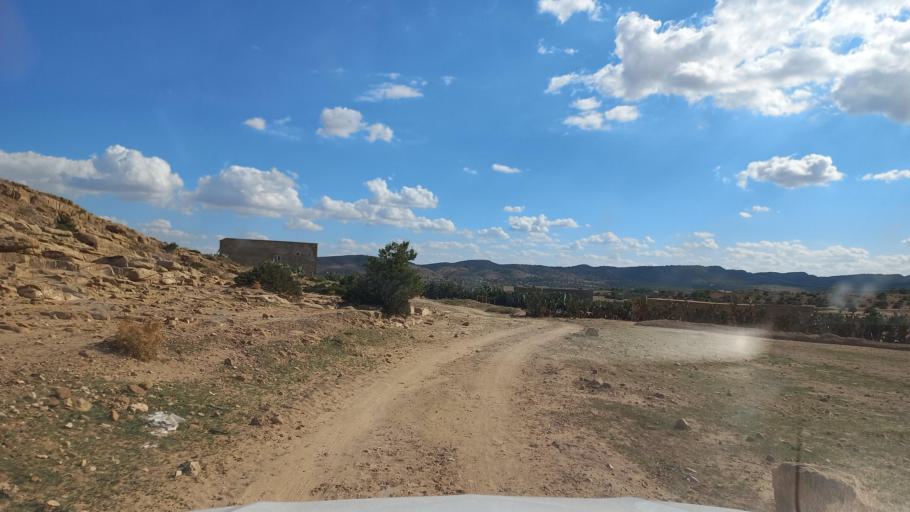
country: TN
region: Al Qasrayn
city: Sbiba
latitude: 35.4073
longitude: 8.9971
